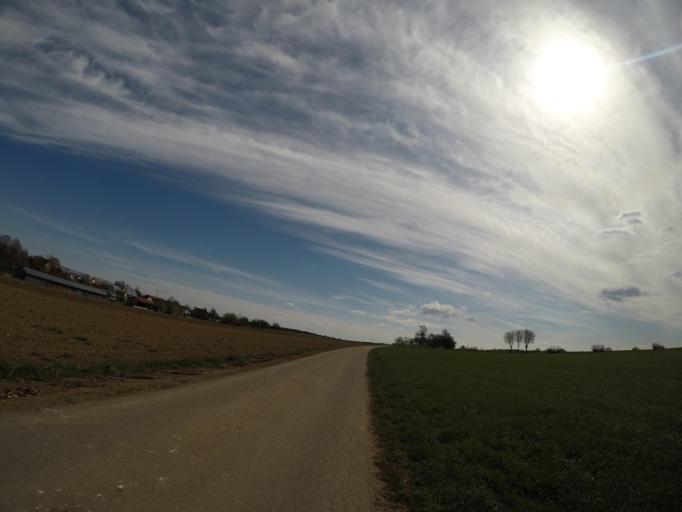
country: DE
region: Baden-Wuerttemberg
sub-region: Tuebingen Region
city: Mehrstetten
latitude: 48.3464
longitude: 9.6047
